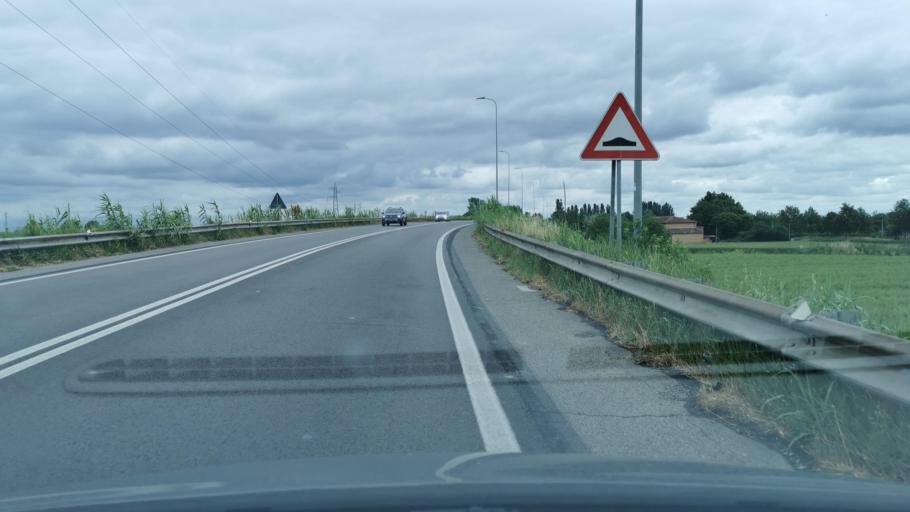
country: IT
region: Emilia-Romagna
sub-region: Provincia di Ravenna
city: Granarolo
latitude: 44.3675
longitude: 11.9380
